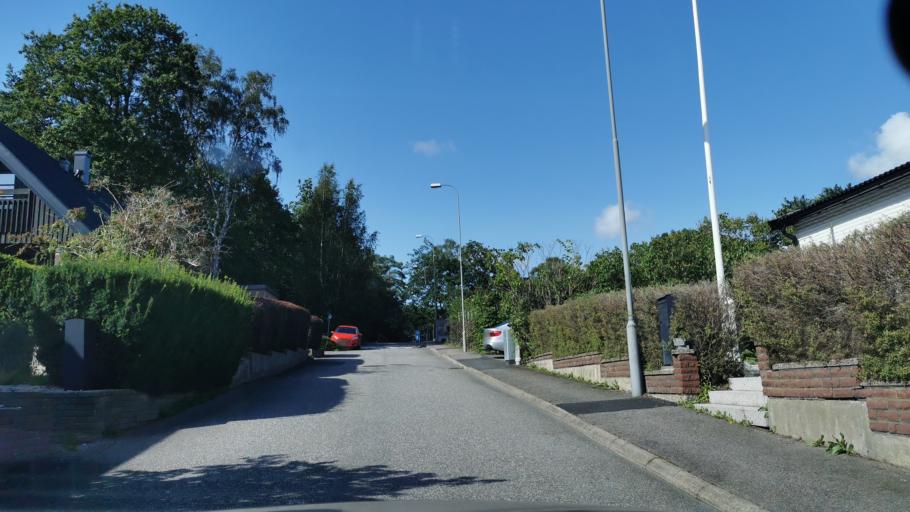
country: SE
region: Vaestra Goetaland
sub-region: Goteborg
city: Majorna
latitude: 57.6405
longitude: 11.9125
